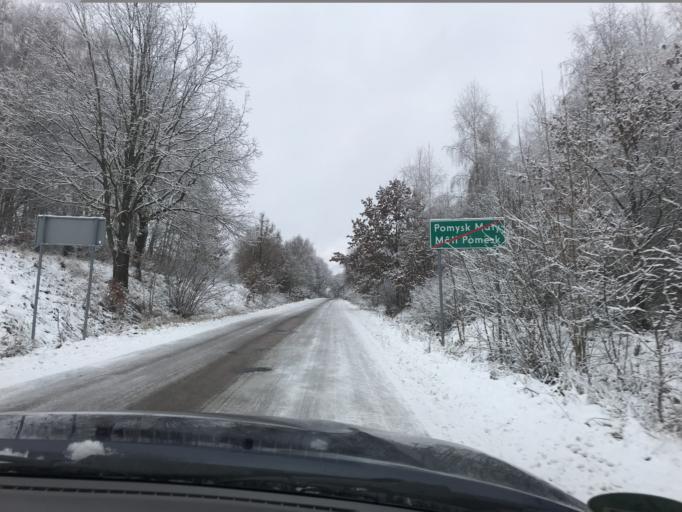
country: PL
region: Pomeranian Voivodeship
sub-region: Powiat bytowski
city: Bytow
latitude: 54.2223
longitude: 17.5644
